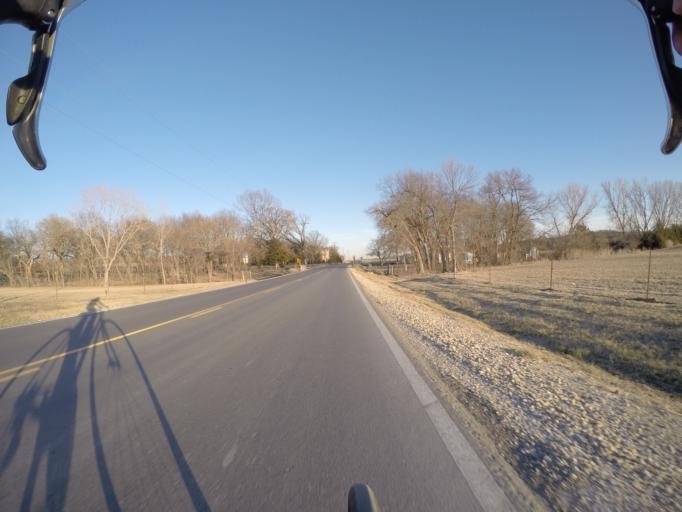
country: US
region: Kansas
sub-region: Riley County
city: Ogden
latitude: 39.2207
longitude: -96.7018
